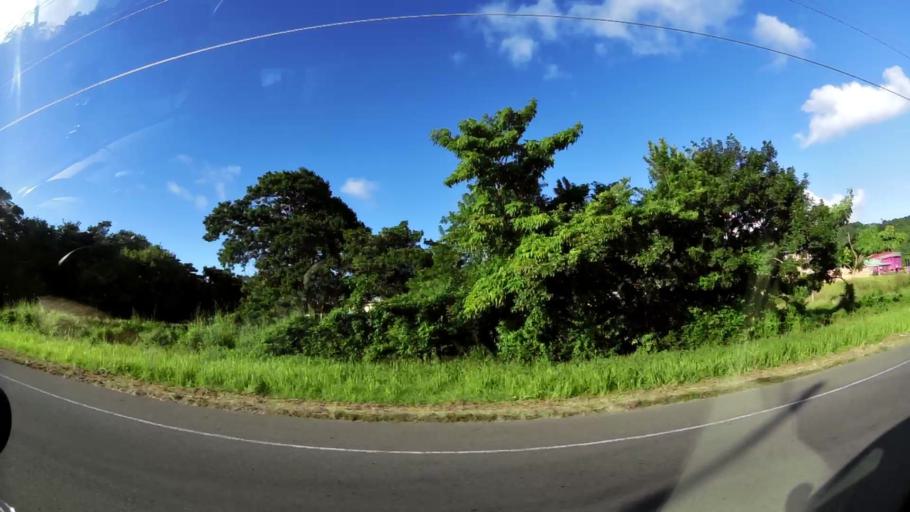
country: TT
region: Tobago
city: Scarborough
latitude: 11.1799
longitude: -60.7118
